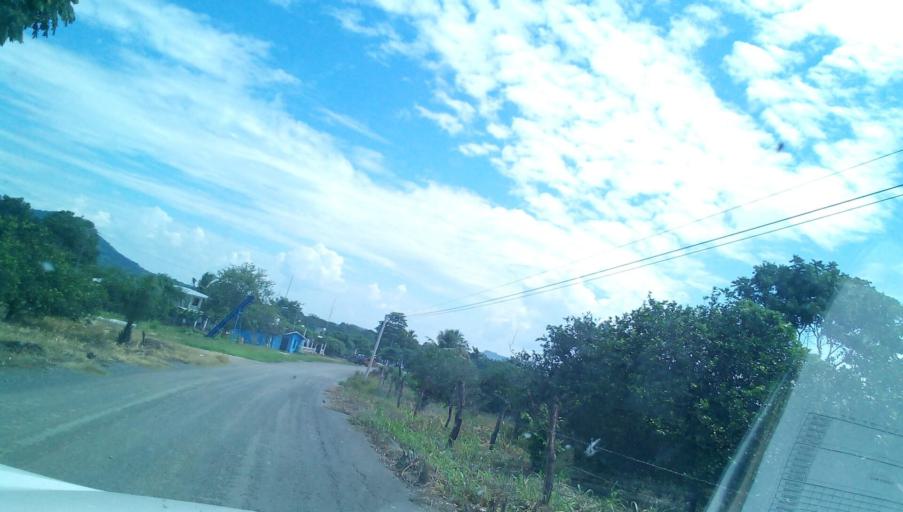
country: MX
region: Veracruz
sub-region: Alamo Temapache
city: Vegas de la Soledad y Soledad Dos
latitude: 20.9010
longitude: -97.9427
